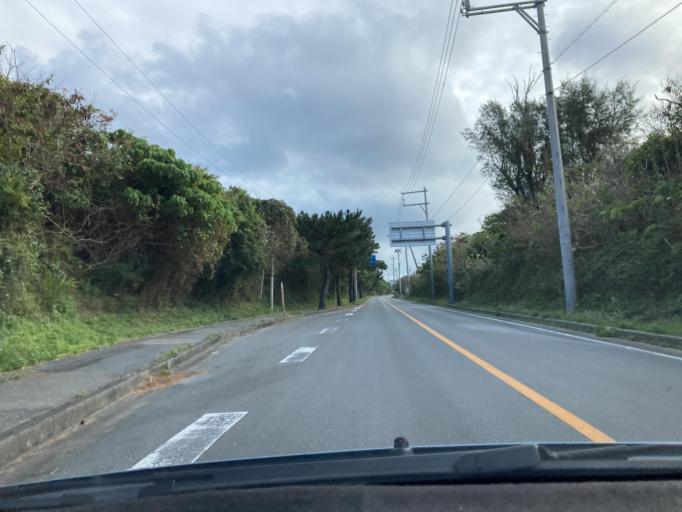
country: JP
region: Okinawa
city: Nago
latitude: 26.8662
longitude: 128.2572
